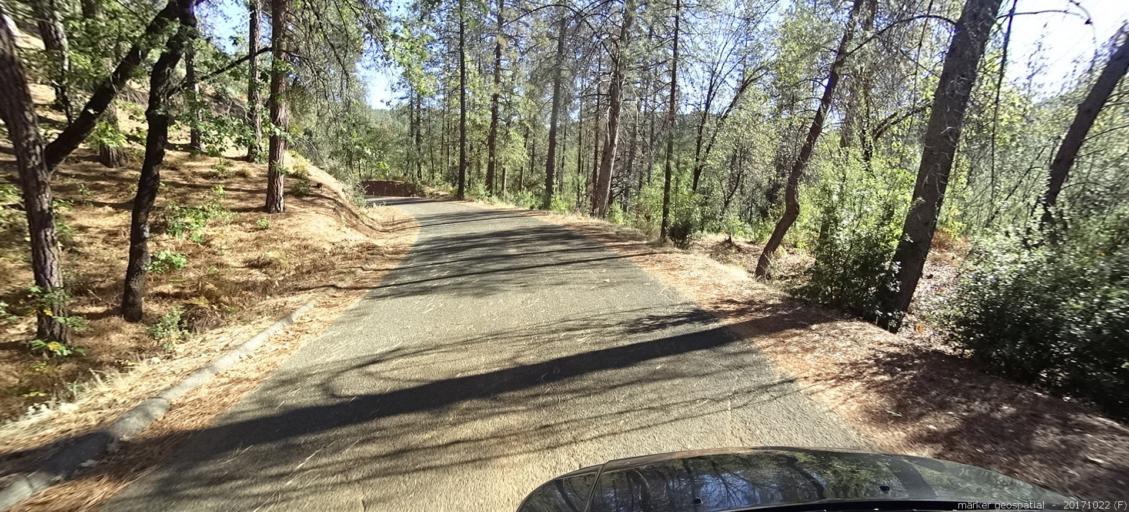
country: US
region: California
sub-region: Shasta County
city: Shasta Lake
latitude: 40.8823
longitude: -122.3688
